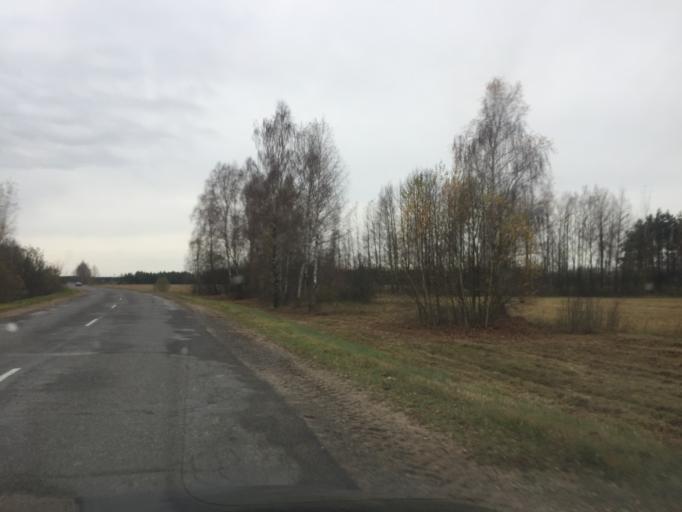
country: BY
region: Mogilev
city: Drybin
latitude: 54.1025
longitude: 31.0952
